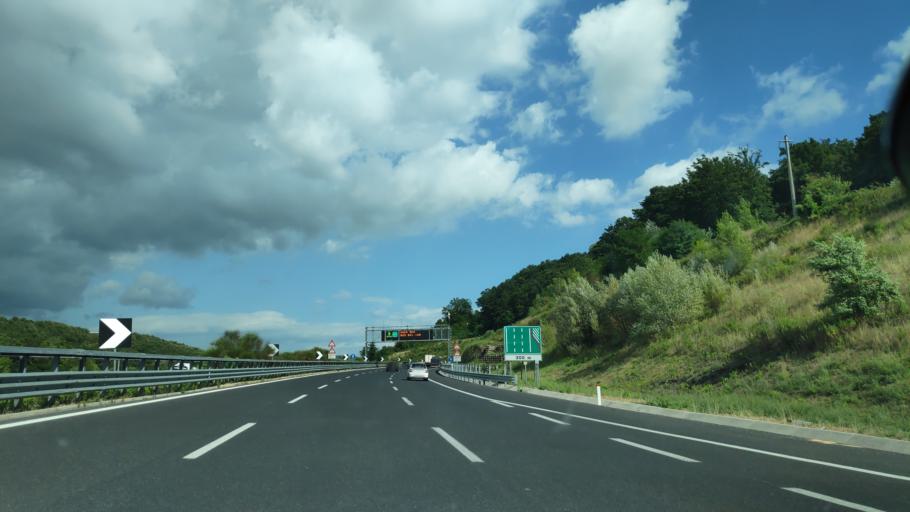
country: IT
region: Campania
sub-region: Provincia di Salerno
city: Contursi Terme
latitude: 40.6280
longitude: 15.2336
